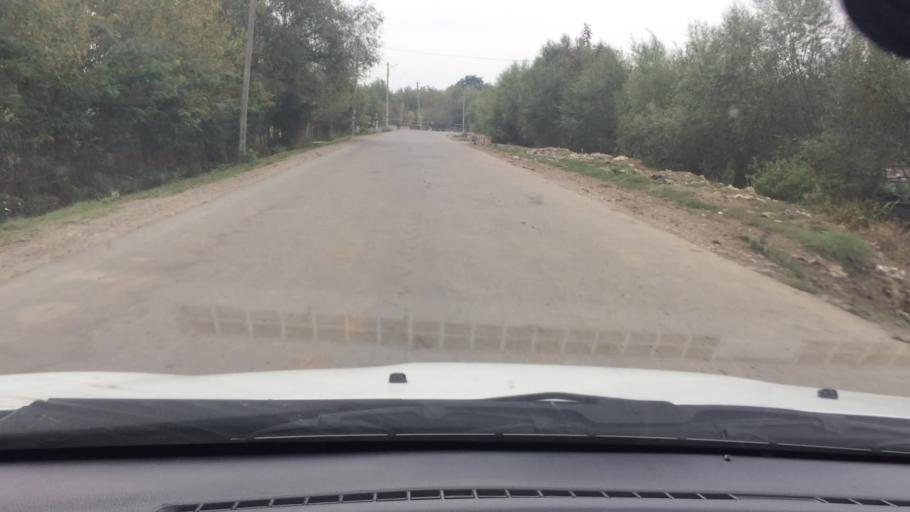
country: AM
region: Tavush
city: Berdavan
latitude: 41.3488
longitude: 44.9752
